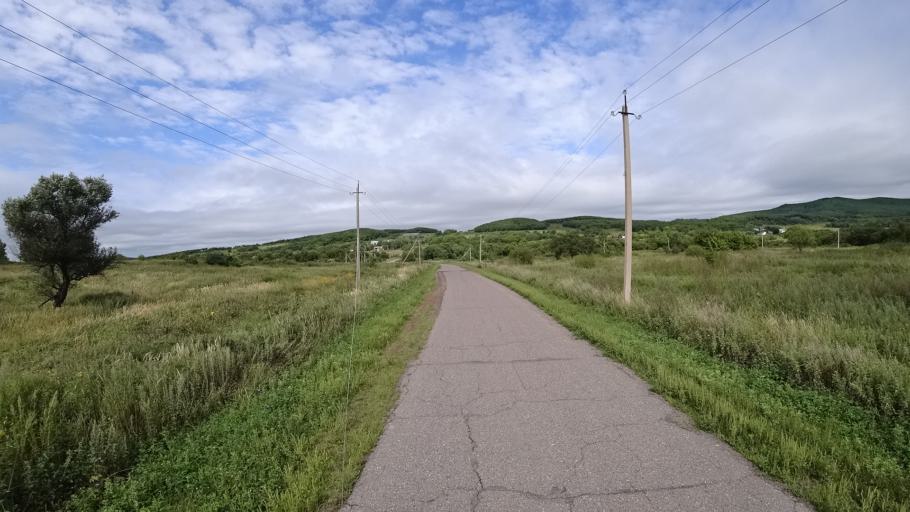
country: RU
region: Primorskiy
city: Lyalichi
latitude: 44.1333
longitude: 132.3878
